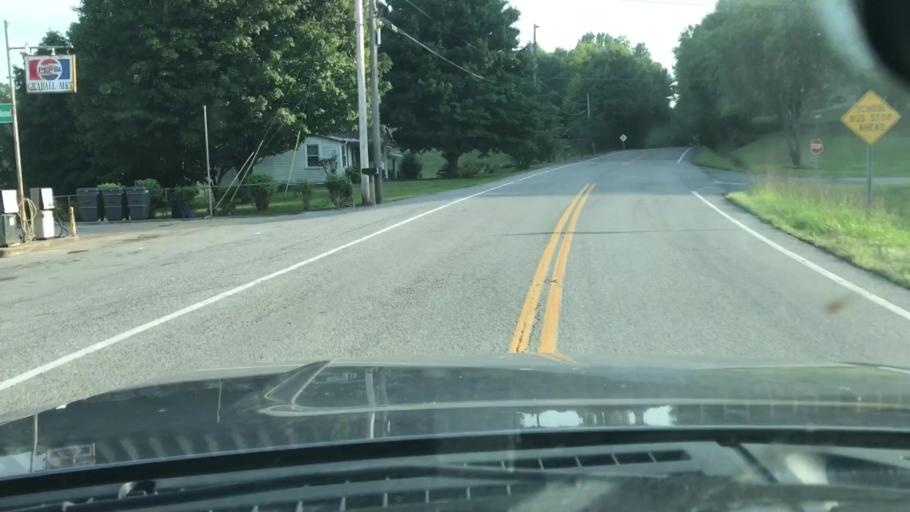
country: US
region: Tennessee
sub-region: Sumner County
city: Gallatin
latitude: 36.4809
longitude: -86.4383
